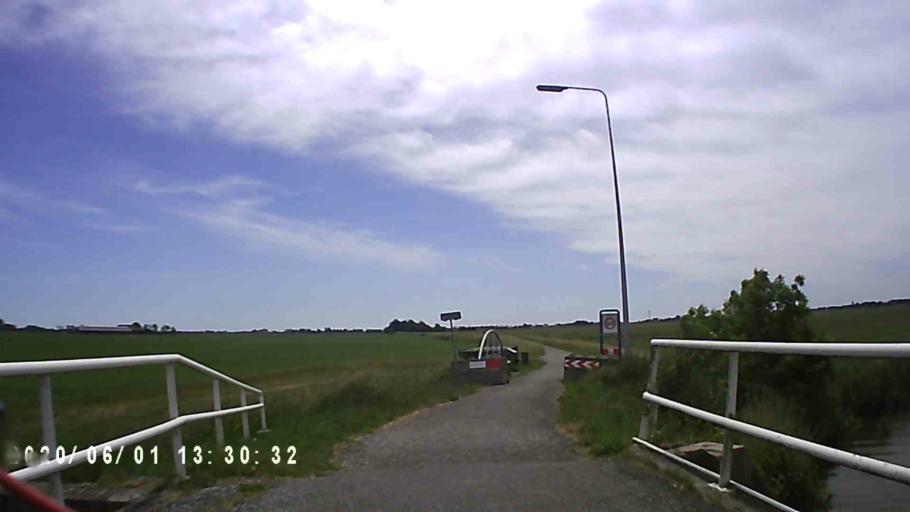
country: NL
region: Friesland
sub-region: Gemeente Littenseradiel
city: Wommels
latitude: 53.0996
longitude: 5.5674
